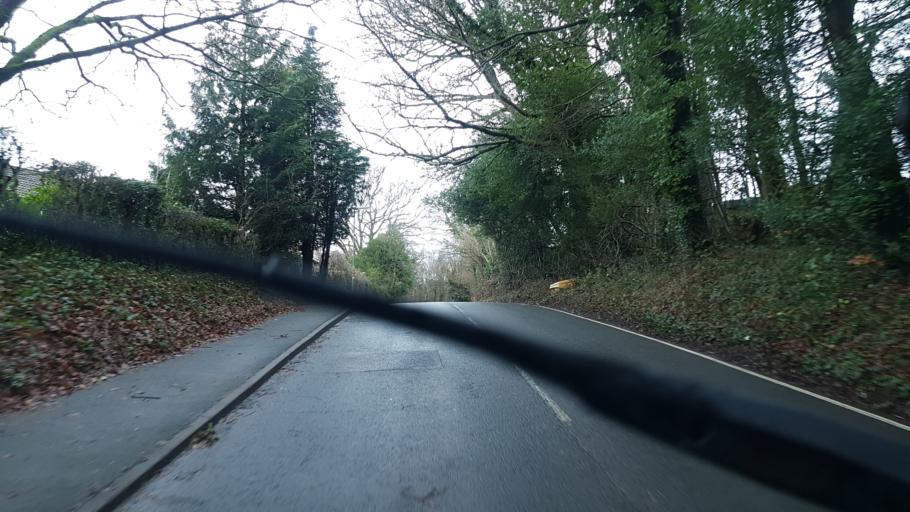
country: GB
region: England
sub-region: Surrey
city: Hindhead
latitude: 51.0904
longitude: -0.7483
